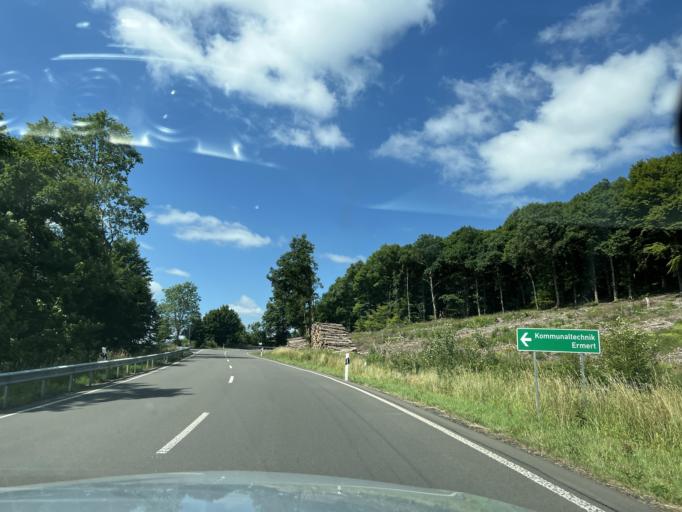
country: DE
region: North Rhine-Westphalia
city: Freudenberg
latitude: 50.9229
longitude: 7.8781
